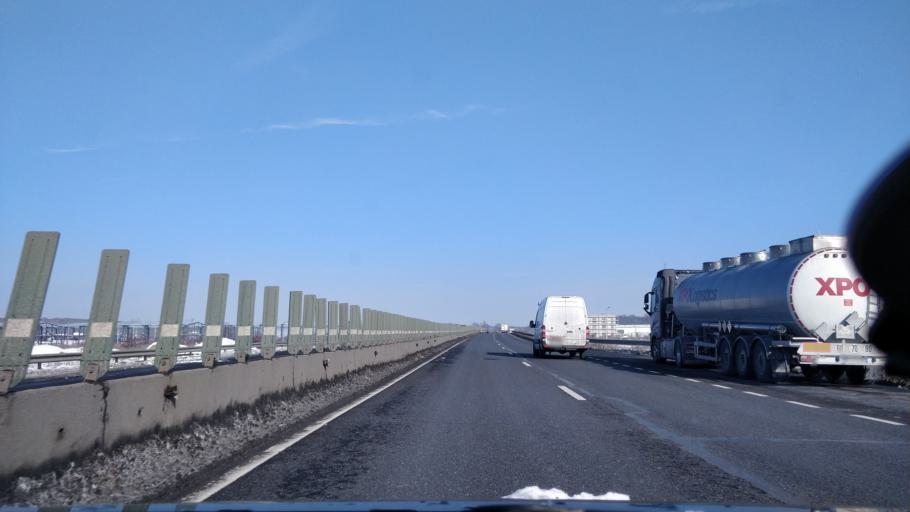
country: RO
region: Ilfov
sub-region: Comuna Chitila
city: Chitila
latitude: 44.5053
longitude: 26.0044
